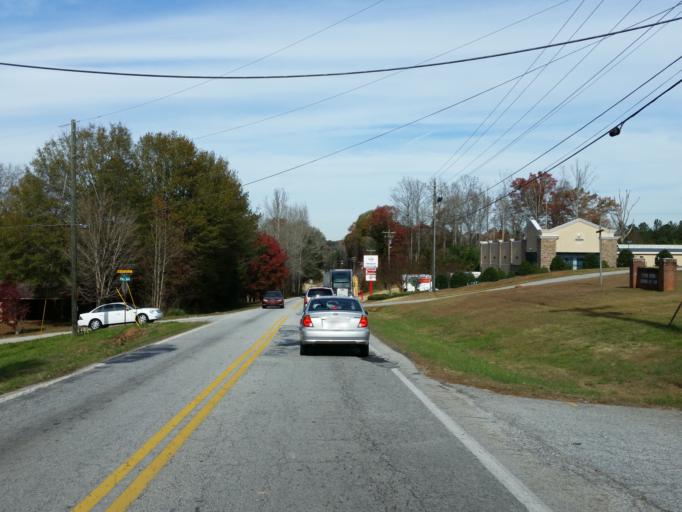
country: US
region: Georgia
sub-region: Douglas County
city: Lithia Springs
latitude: 33.7590
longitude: -84.6510
